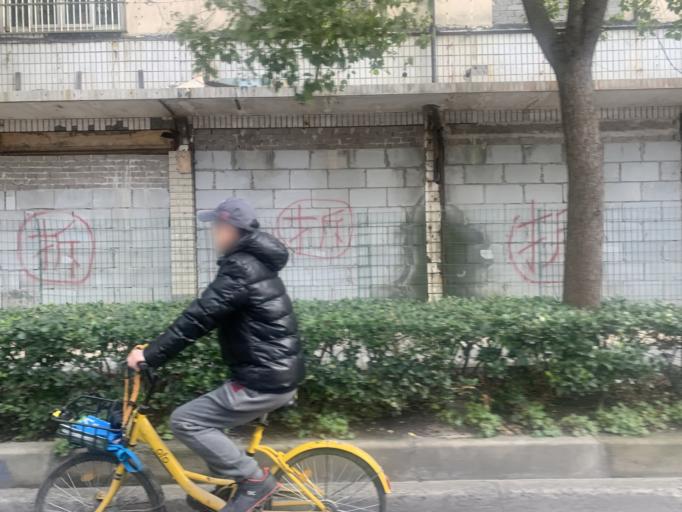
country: CN
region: Shanghai Shi
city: Huamu
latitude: 31.1841
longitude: 121.5152
